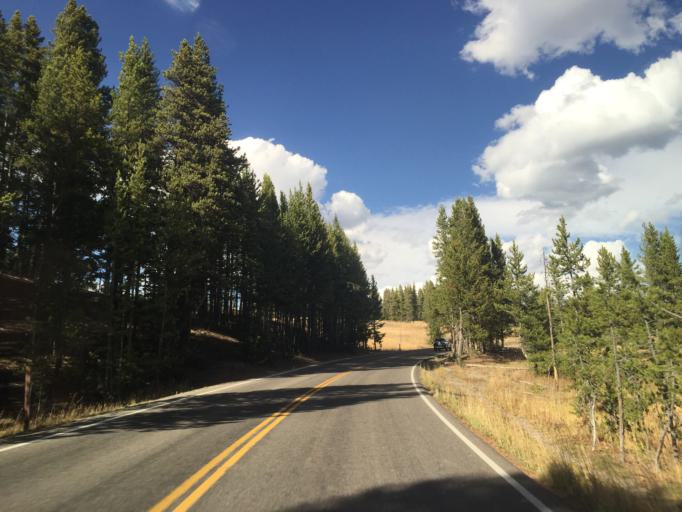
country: US
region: Montana
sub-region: Gallatin County
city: West Yellowstone
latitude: 44.7105
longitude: -110.5053
